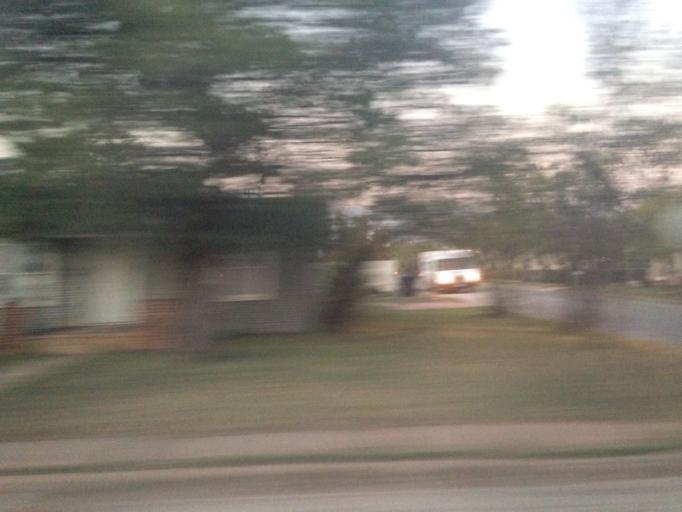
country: US
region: Texas
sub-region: Taylor County
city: Abilene
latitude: 32.4474
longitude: -99.7560
